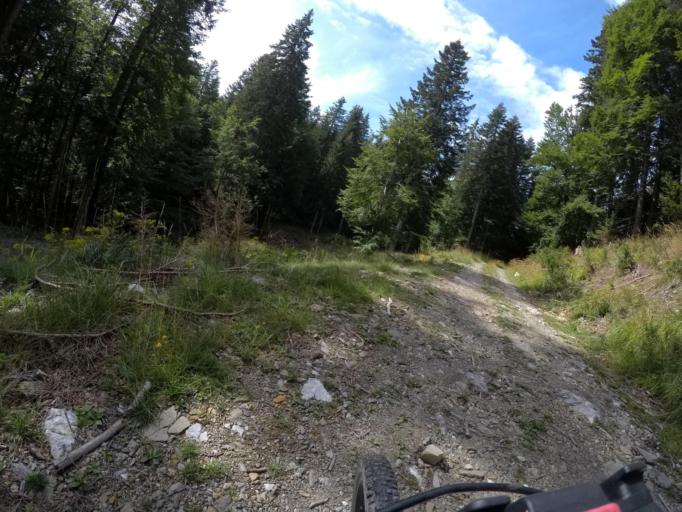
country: IT
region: Friuli Venezia Giulia
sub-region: Provincia di Udine
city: Paularo
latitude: 46.5112
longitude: 13.2050
